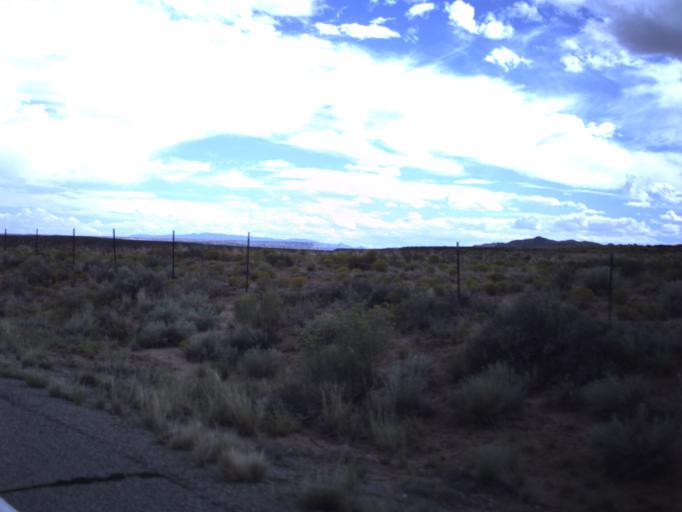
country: US
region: Utah
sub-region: San Juan County
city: Blanding
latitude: 37.2952
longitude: -109.4252
